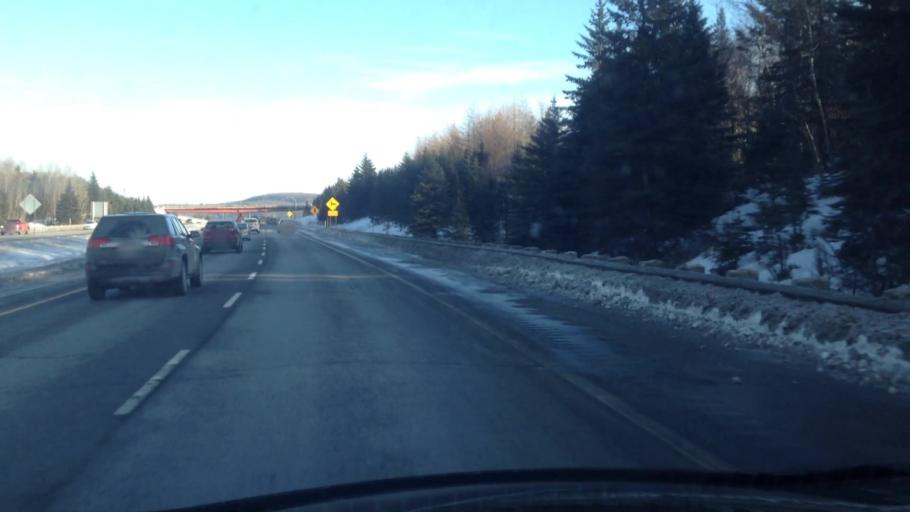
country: CA
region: Quebec
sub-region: Laurentides
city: Prevost
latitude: 45.8858
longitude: -74.1268
